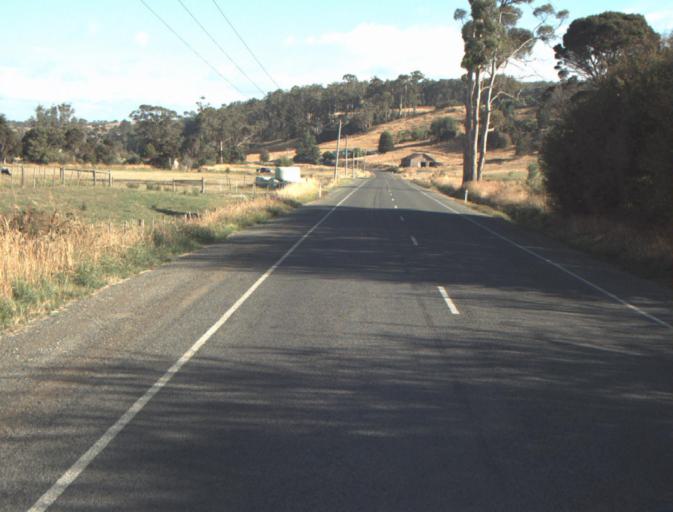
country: AU
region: Tasmania
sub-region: Launceston
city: Mayfield
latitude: -41.2407
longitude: 147.2161
